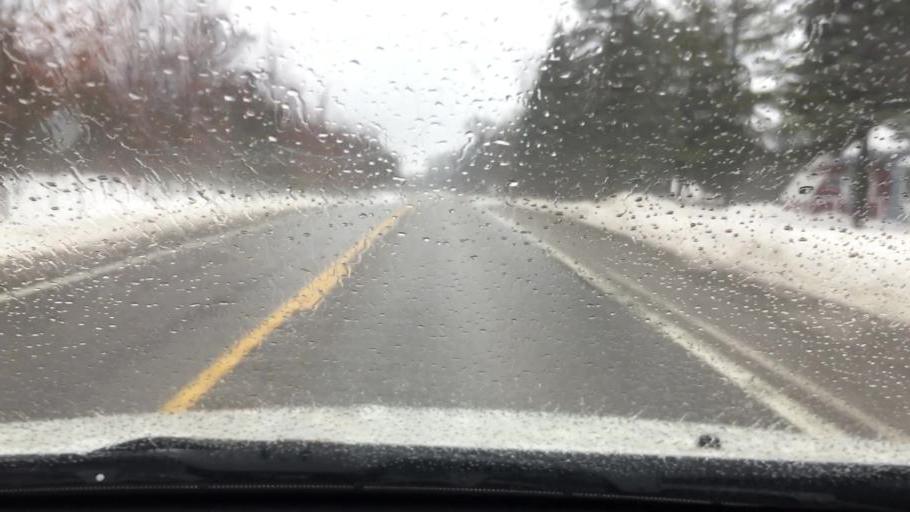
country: US
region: Michigan
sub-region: Charlevoix County
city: East Jordan
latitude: 45.1883
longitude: -85.1649
